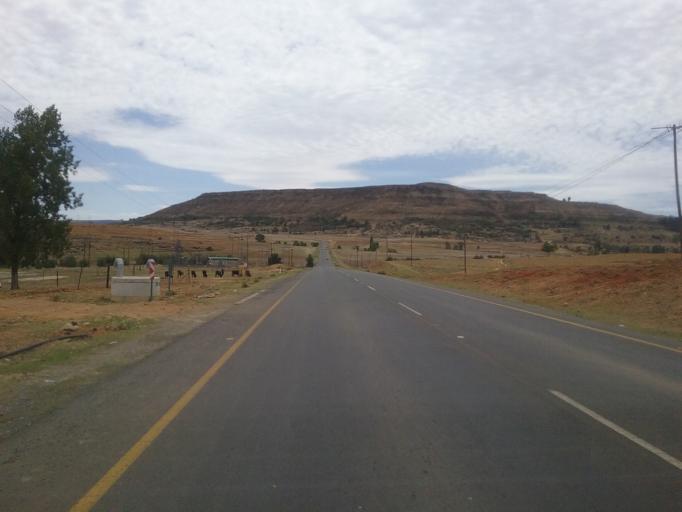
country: LS
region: Maseru
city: Nako
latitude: -29.6188
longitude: 27.4978
